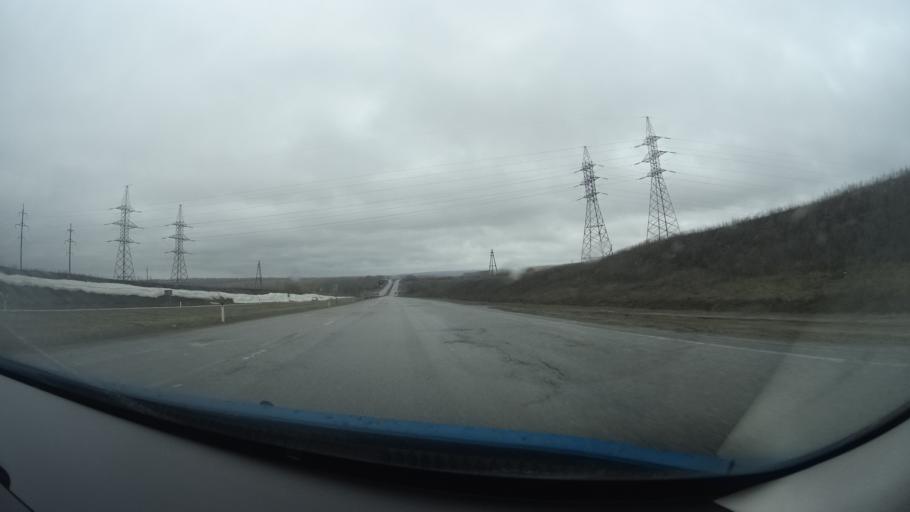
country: RU
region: Bashkortostan
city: Alekseyevka
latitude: 54.7308
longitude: 55.0225
